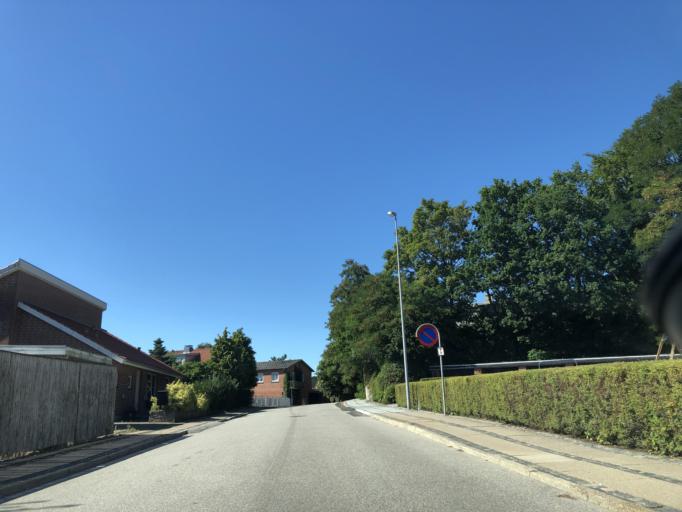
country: DK
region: North Denmark
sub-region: Mariagerfjord Kommune
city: Hobro
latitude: 56.6417
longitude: 9.7970
